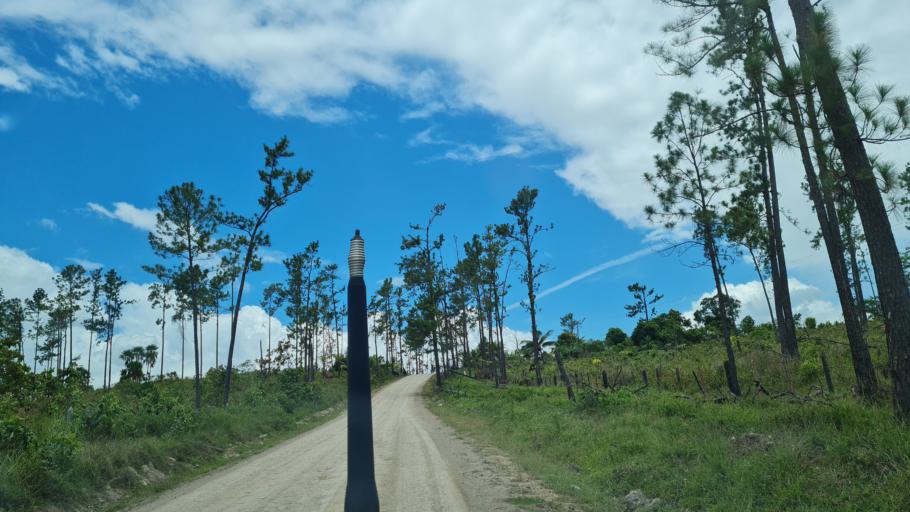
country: NI
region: Atlantico Sur
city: La Cruz de Rio Grande
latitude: 13.5741
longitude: -84.3230
